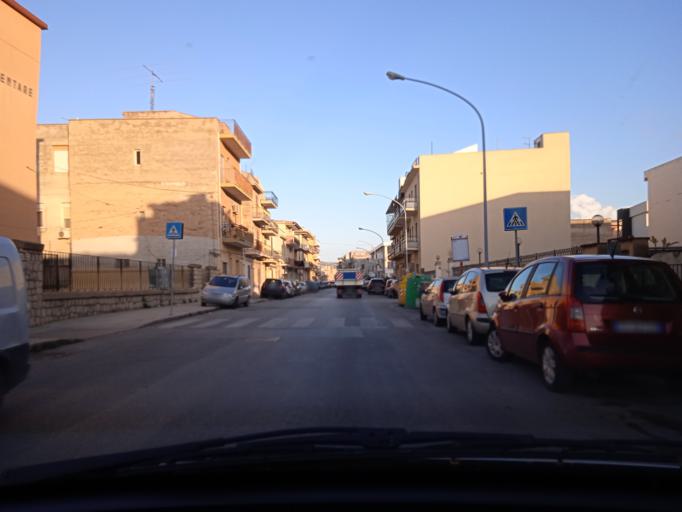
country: IT
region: Sicily
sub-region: Palermo
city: Ciaculli
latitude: 38.0909
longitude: 13.4143
